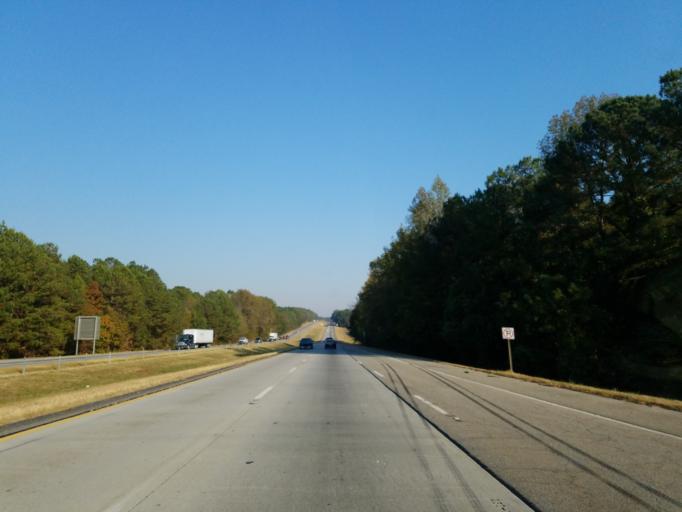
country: US
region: Georgia
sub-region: Bibb County
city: West Point
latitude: 32.9398
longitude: -83.7751
